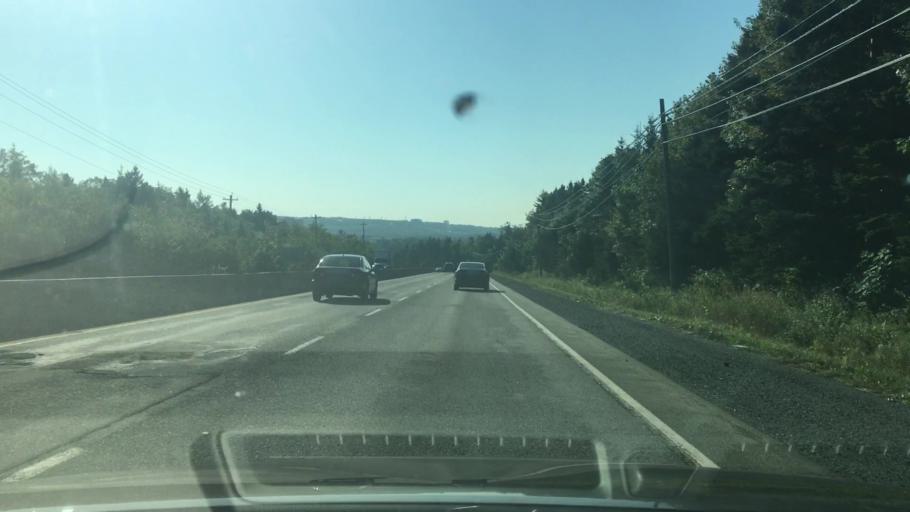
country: CA
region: Nova Scotia
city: Dartmouth
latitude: 44.7109
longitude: -63.6270
